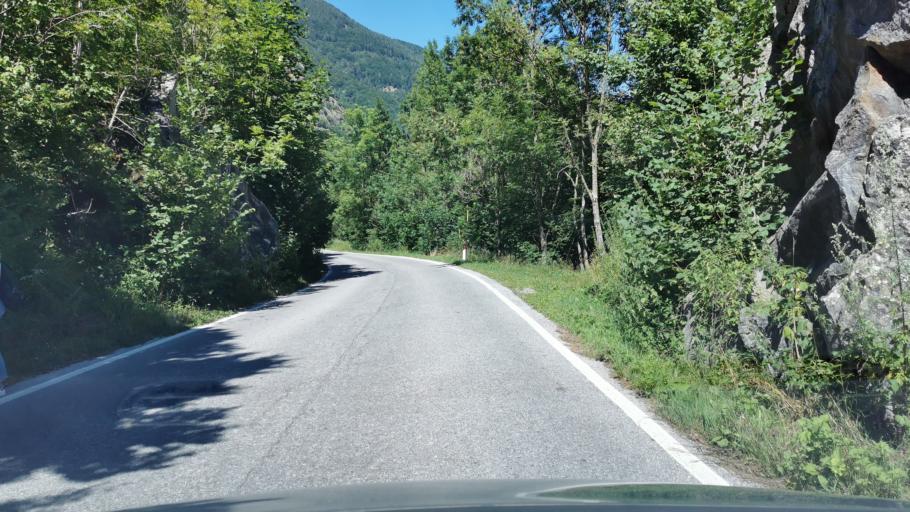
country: IT
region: Piedmont
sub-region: Provincia di Cuneo
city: Demonte
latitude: 44.2395
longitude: 7.3173
